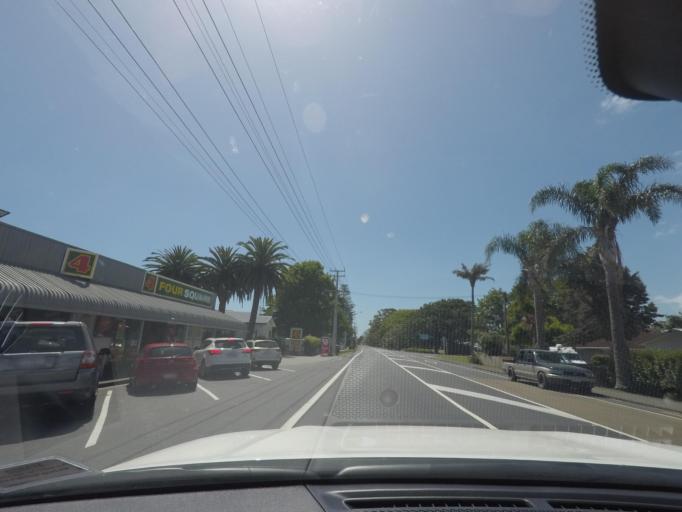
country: NZ
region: Auckland
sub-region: Auckland
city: Parakai
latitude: -36.6614
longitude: 174.4339
